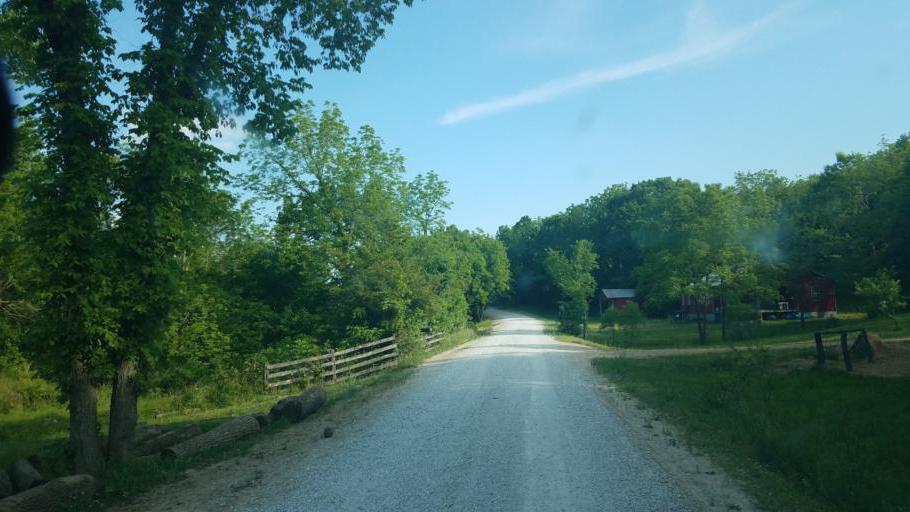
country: US
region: Missouri
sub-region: Moniteau County
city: California
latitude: 38.7451
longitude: -92.6282
